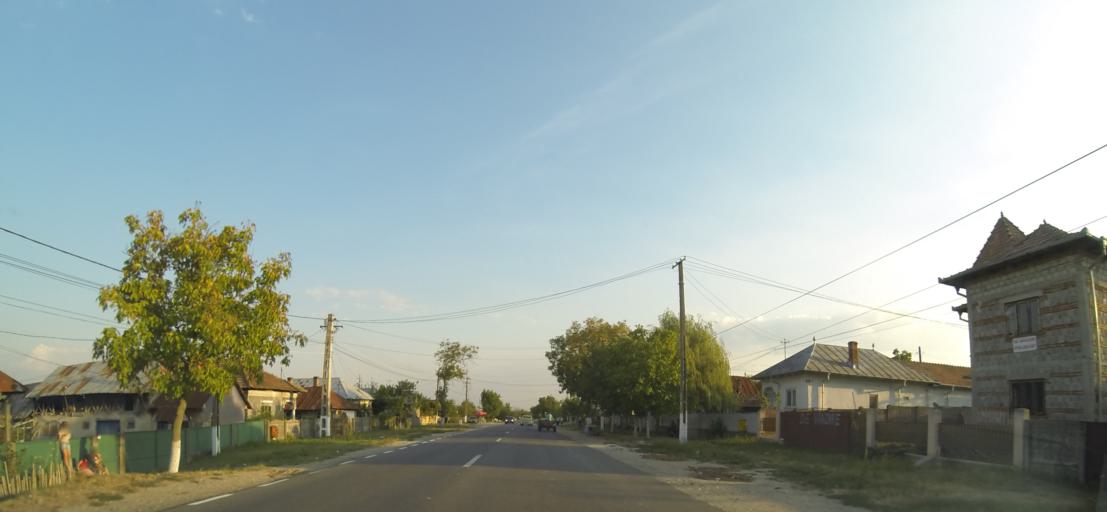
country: RO
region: Valcea
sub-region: Comuna Prundeni
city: Prundeni
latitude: 44.7326
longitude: 24.2504
